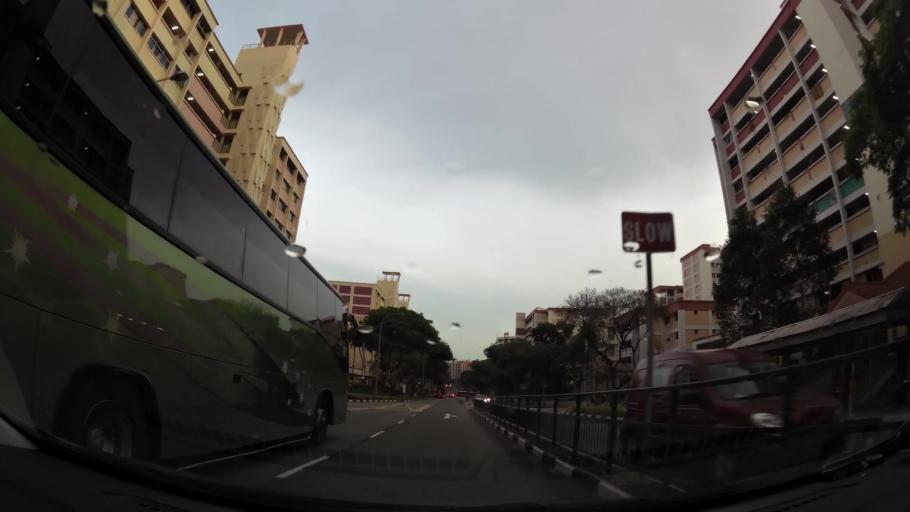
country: MY
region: Johor
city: Kampung Pasir Gudang Baru
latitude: 1.4344
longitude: 103.8393
